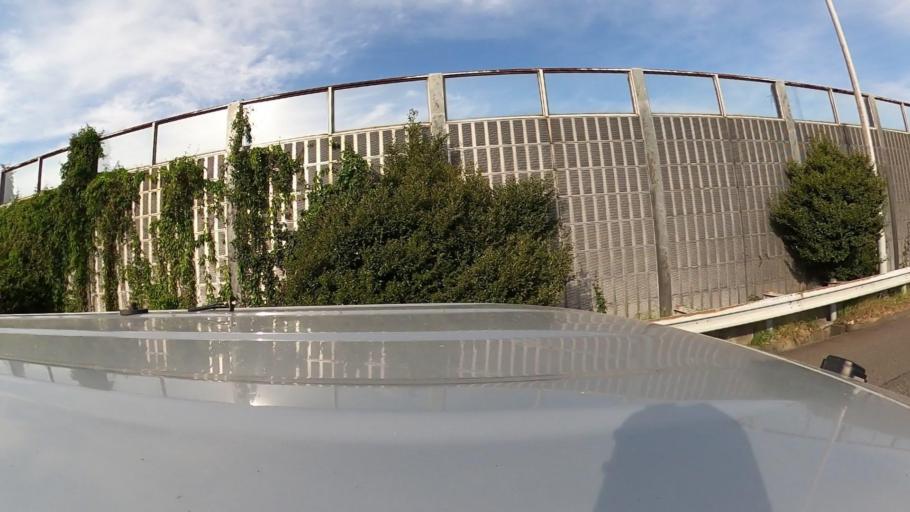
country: JP
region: Saitama
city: Oi
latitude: 35.8527
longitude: 139.5002
